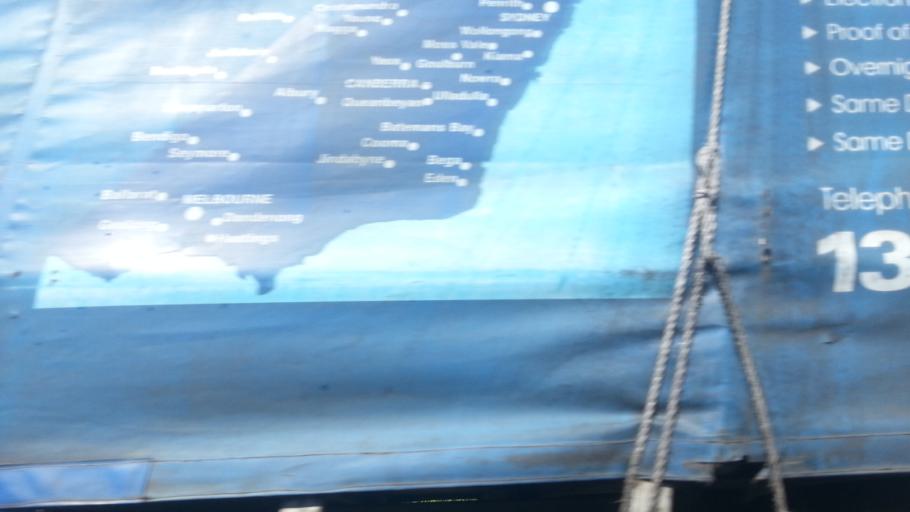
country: AU
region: New South Wales
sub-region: Wollongong
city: Fairy Meadow
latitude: -34.4016
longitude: 150.8879
